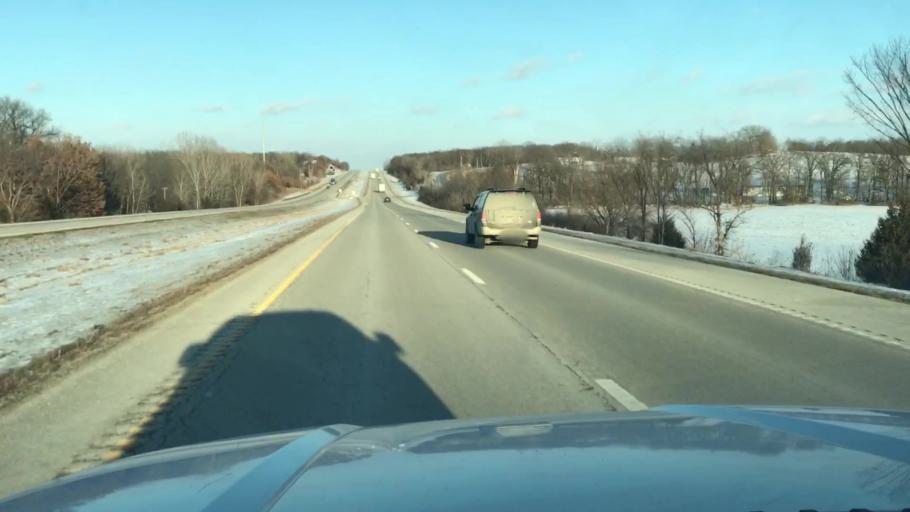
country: US
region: Missouri
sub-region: Clinton County
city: Gower
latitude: 39.7495
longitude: -94.5996
